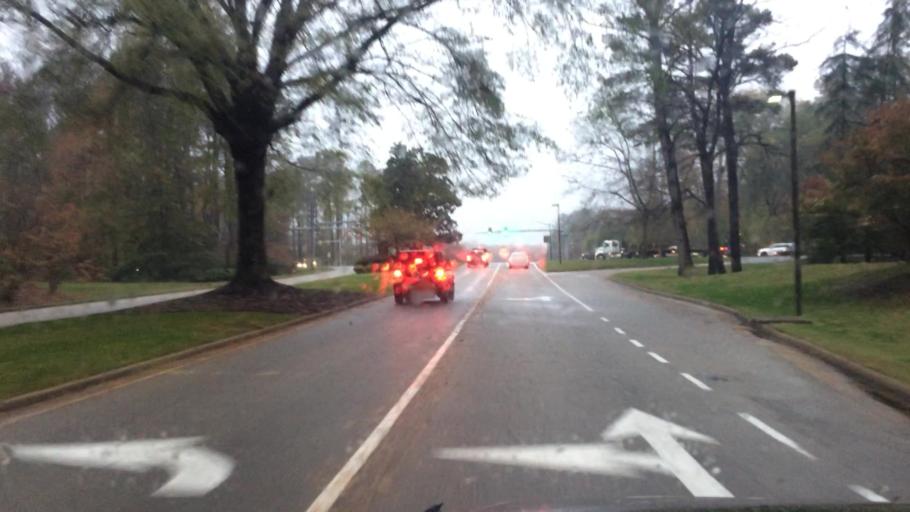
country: US
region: Virginia
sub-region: City of Williamsburg
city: Williamsburg
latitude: 37.2463
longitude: -76.6814
